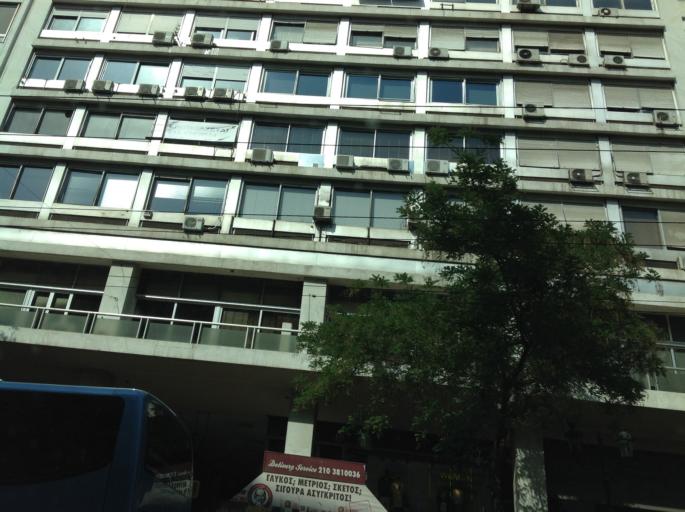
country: GR
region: Attica
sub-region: Nomarchia Athinas
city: Athens
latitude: 37.9833
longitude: 23.7304
